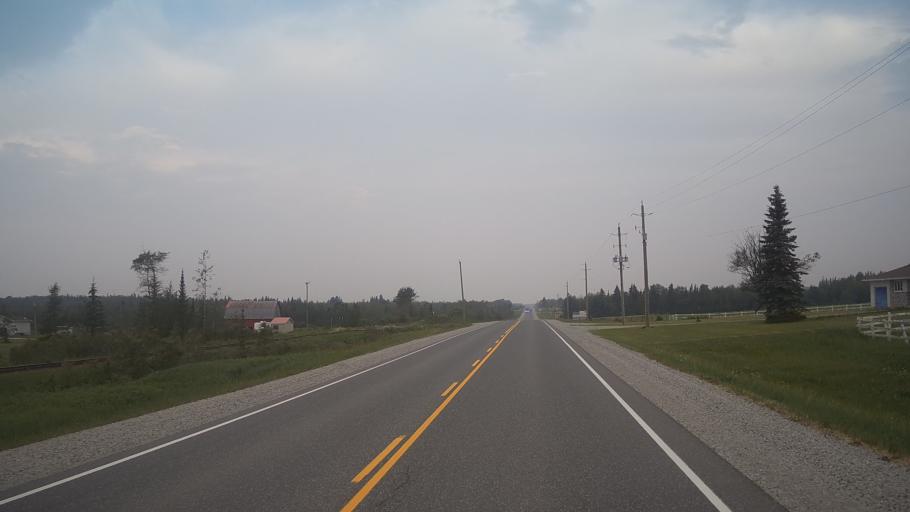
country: CA
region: Ontario
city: Hearst
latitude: 49.6719
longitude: -83.5286
